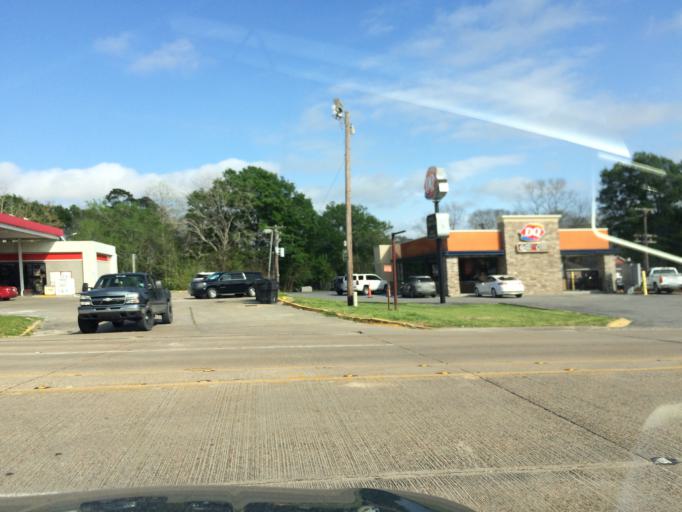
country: US
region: Louisiana
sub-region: Jefferson Davis Parish
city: Welsh
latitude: 30.2435
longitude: -92.8218
